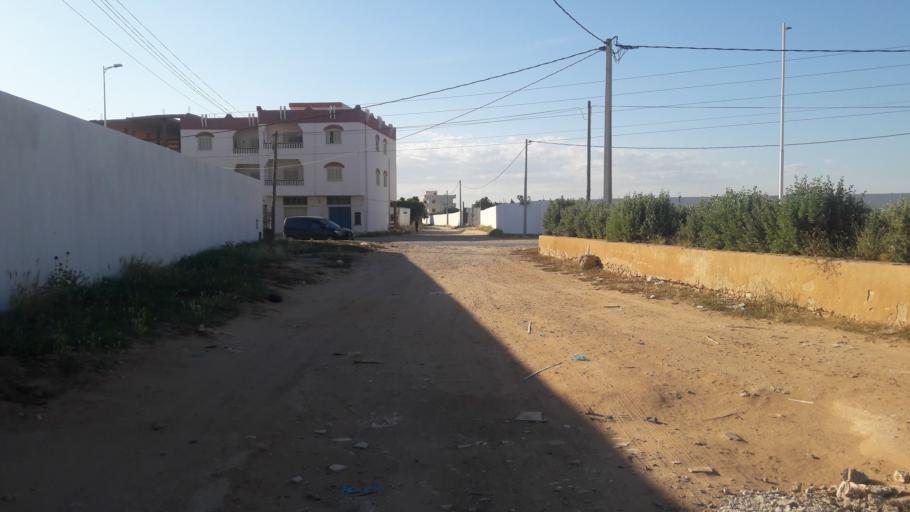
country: TN
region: Safaqis
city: Sfax
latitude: 34.8148
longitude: 10.7407
